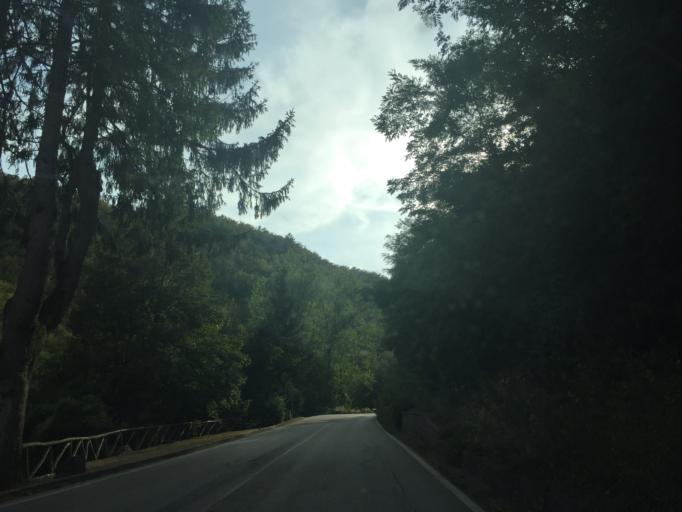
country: IT
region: Tuscany
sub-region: Provincia di Pistoia
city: Campo Tizzoro
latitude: 44.0060
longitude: 10.8464
